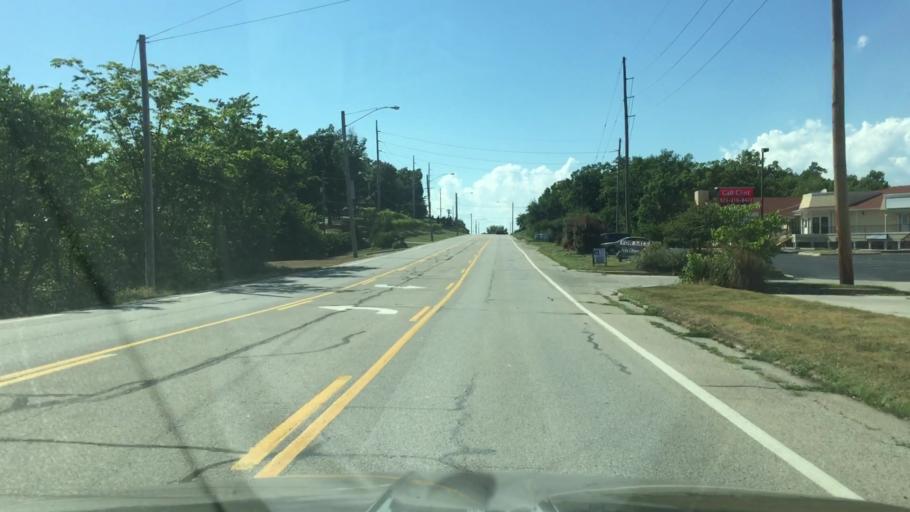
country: US
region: Missouri
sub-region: Miller County
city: Lake Ozark
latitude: 38.1835
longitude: -92.6351
